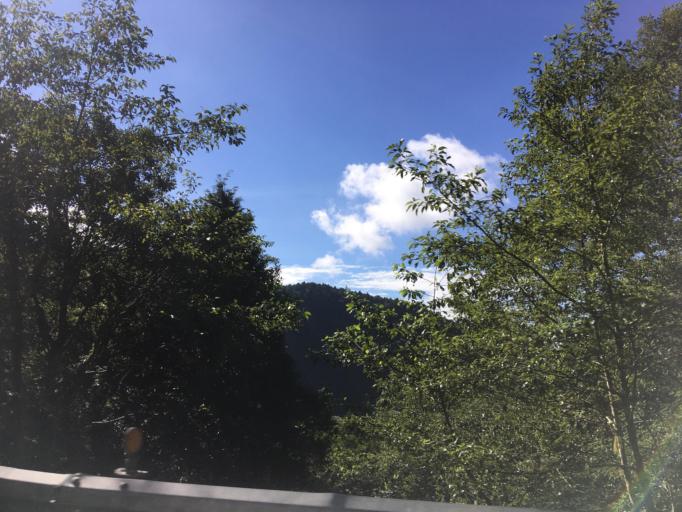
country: TW
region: Taiwan
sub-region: Yilan
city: Yilan
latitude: 24.5164
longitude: 121.5710
